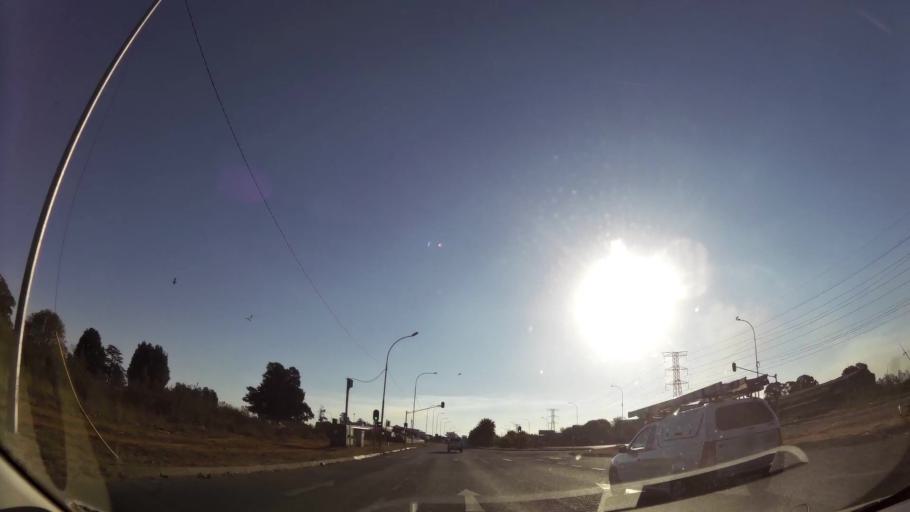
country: ZA
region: Gauteng
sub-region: City of Johannesburg Metropolitan Municipality
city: Roodepoort
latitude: -26.1991
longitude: 27.9391
